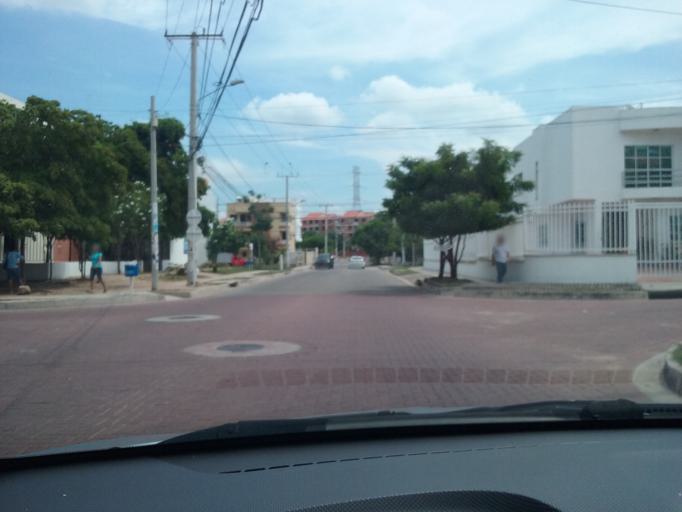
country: CO
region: Atlantico
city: Barranquilla
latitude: 11.0203
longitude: -74.8160
